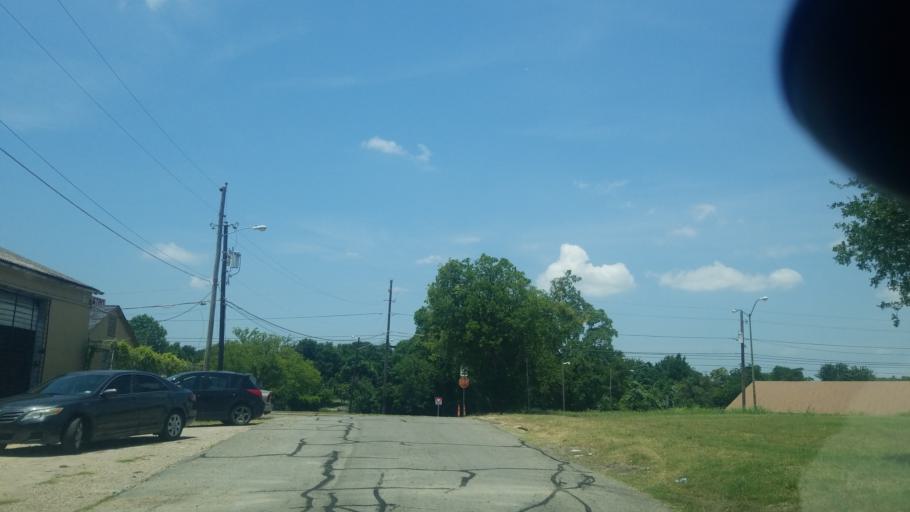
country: US
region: Texas
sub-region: Dallas County
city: Dallas
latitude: 32.7327
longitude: -96.7929
